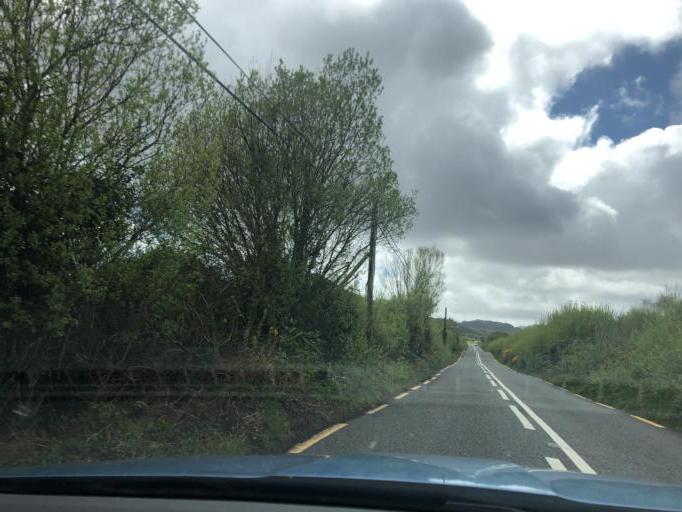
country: IE
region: Munster
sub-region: Ciarrai
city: Killorglin
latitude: 51.8334
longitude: -9.9239
